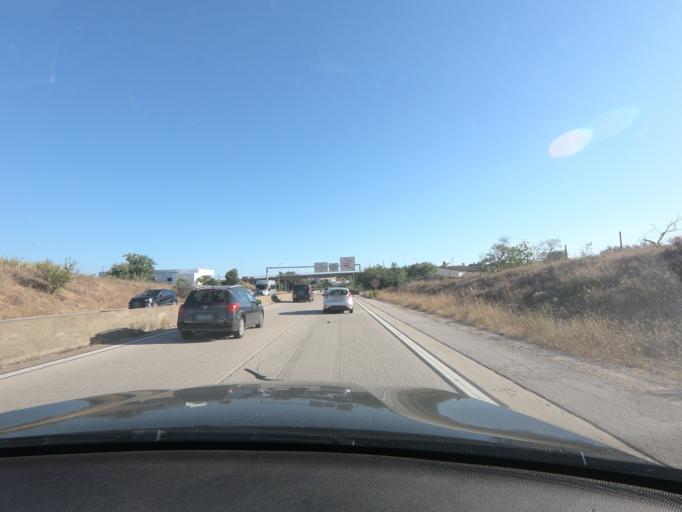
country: PT
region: Faro
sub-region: Faro
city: Santa Barbara de Nexe
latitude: 37.0782
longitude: -7.9789
